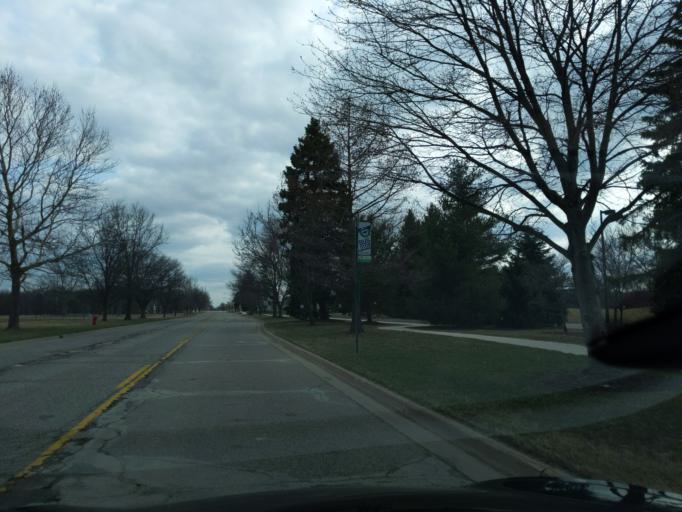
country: US
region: Michigan
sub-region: Ingham County
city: East Lansing
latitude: 42.6942
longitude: -84.4989
